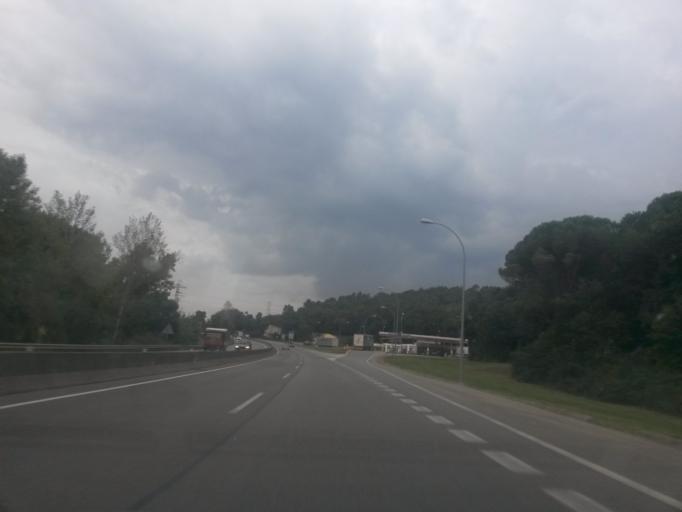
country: ES
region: Catalonia
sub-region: Provincia de Girona
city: Palol de Revardit
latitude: 42.0655
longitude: 2.8126
